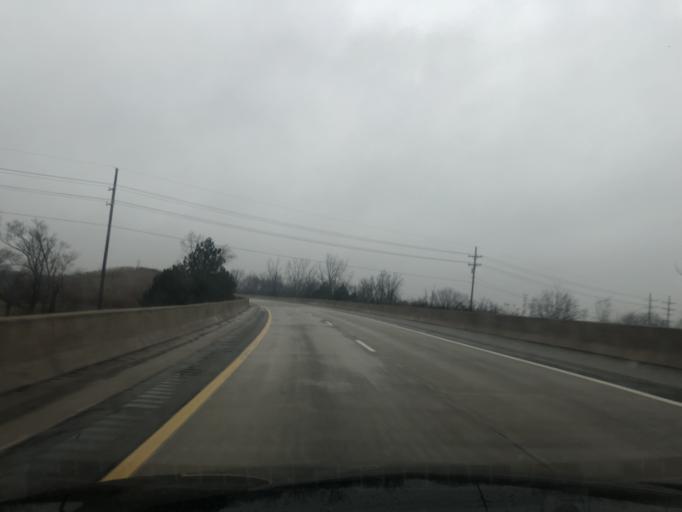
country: US
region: Michigan
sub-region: Wayne County
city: Woodhaven
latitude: 42.1896
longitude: -83.2467
